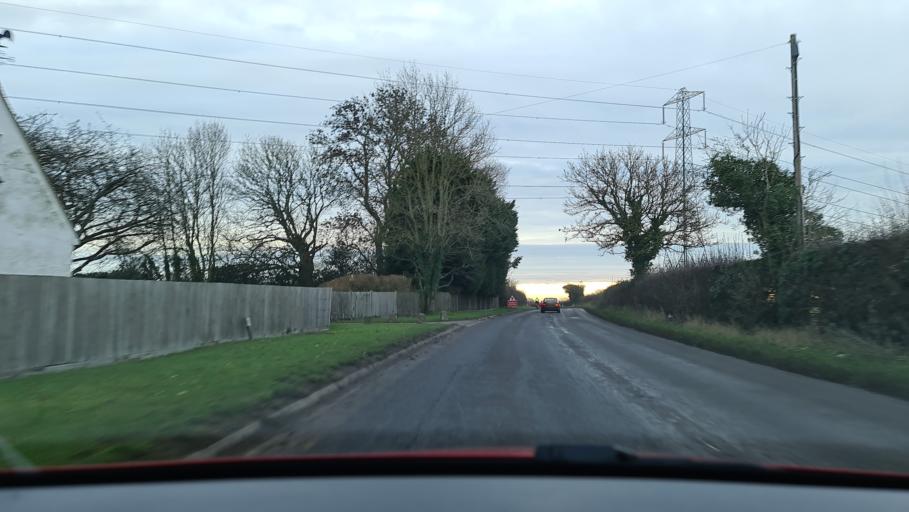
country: GB
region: England
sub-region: Buckinghamshire
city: Great Missenden
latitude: 51.7028
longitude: -0.6893
